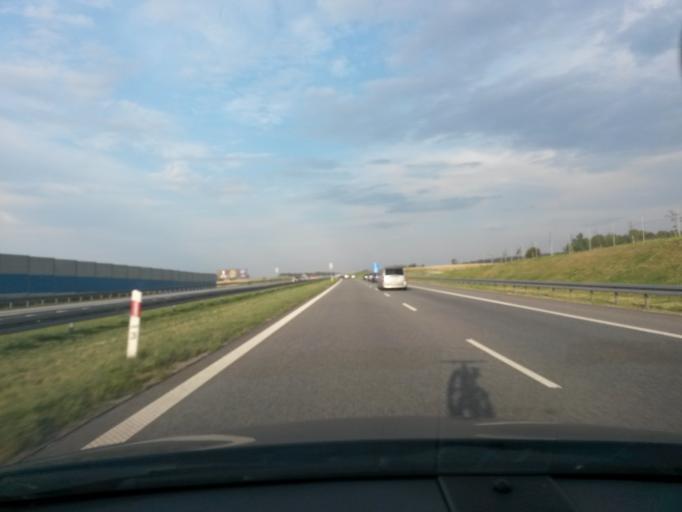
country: PL
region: Lodz Voivodeship
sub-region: Powiat zgierski
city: Glowno
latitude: 51.8969
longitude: 19.6882
